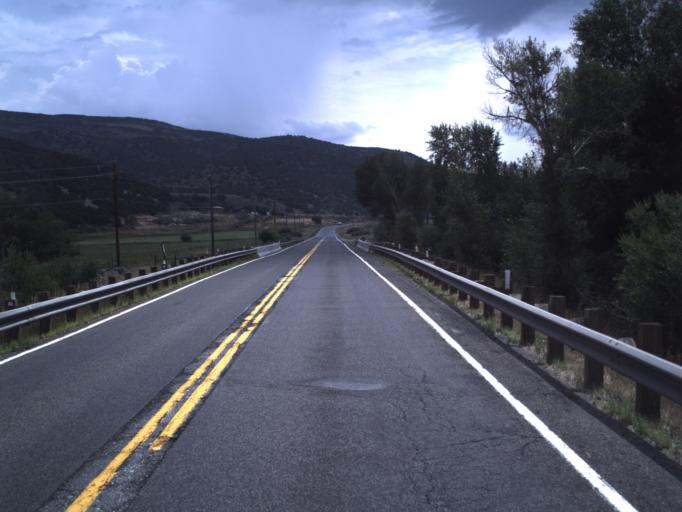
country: US
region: Utah
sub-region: Summit County
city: Oakley
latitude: 40.7511
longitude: -111.3710
